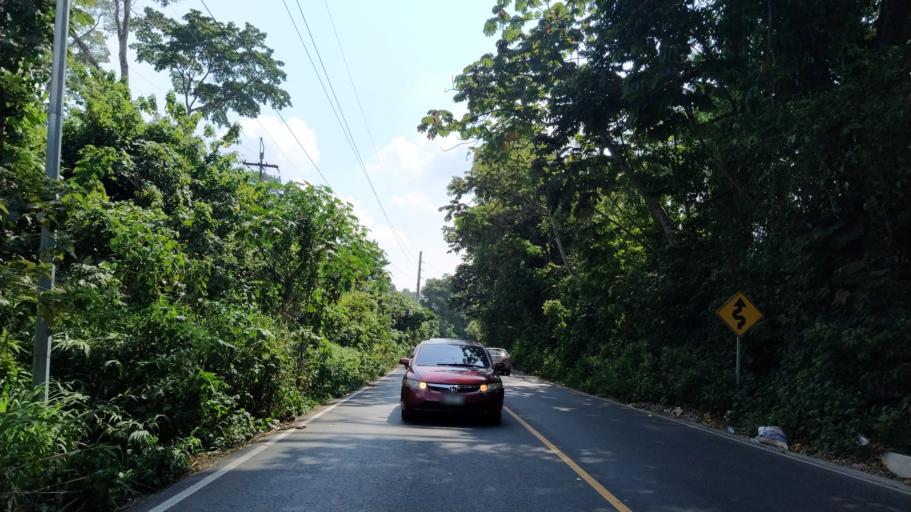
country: GT
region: Retalhuleu
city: San Felipe
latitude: 14.6264
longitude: -91.5852
